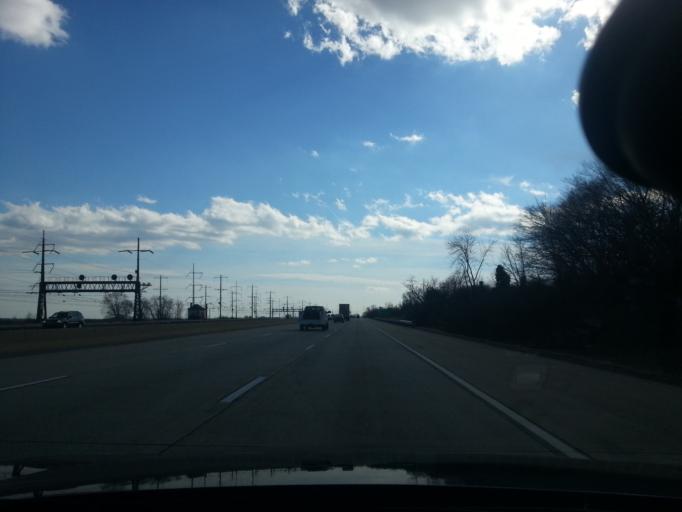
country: US
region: Delaware
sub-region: New Castle County
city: Edgemoor
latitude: 39.7685
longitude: -75.4849
